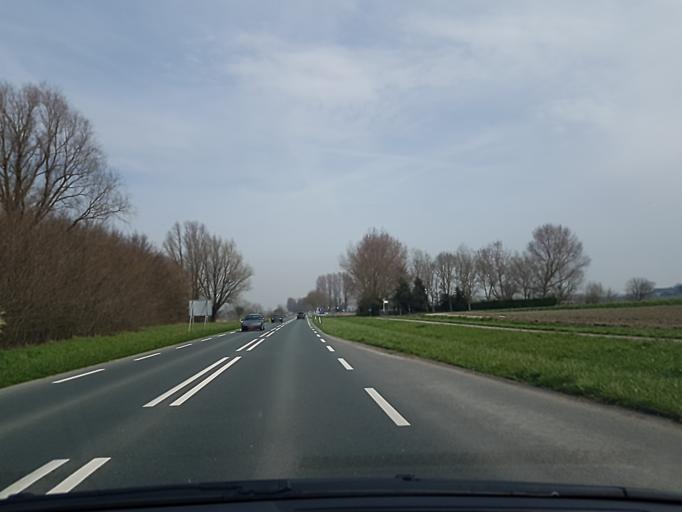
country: NL
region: Zeeland
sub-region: Gemeente Terneuzen
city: Sluiskil
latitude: 51.3103
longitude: 3.8670
